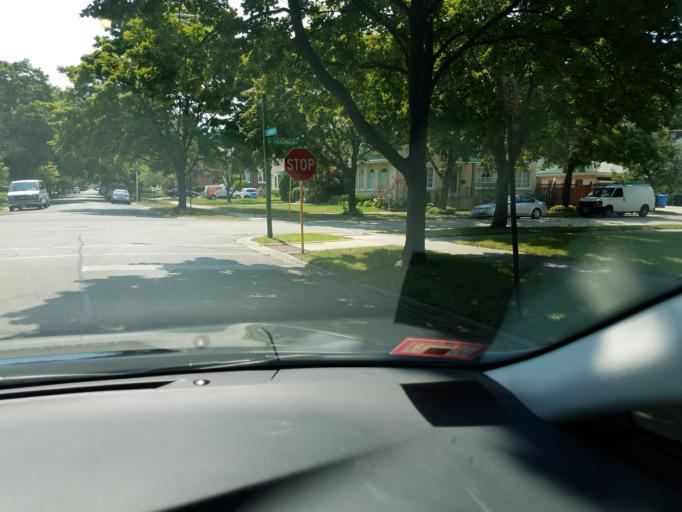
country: US
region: Illinois
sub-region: Cook County
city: Lincolnwood
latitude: 41.9940
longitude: -87.7407
